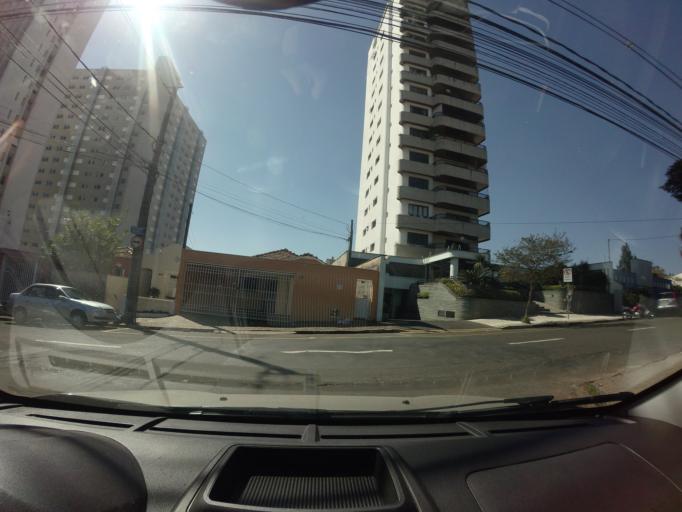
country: BR
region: Sao Paulo
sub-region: Piracicaba
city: Piracicaba
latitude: -22.7184
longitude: -47.6454
